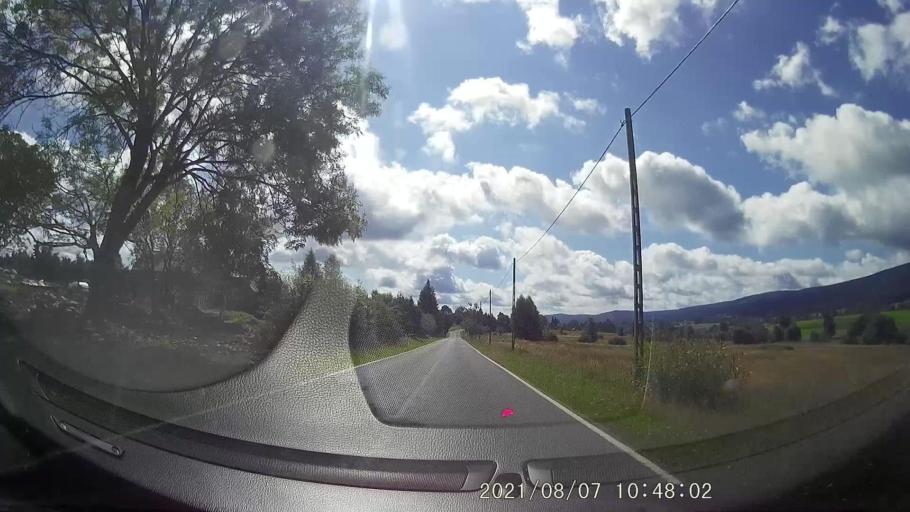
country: PL
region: Lower Silesian Voivodeship
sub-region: Powiat klodzki
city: Szczytna
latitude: 50.3142
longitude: 16.4460
